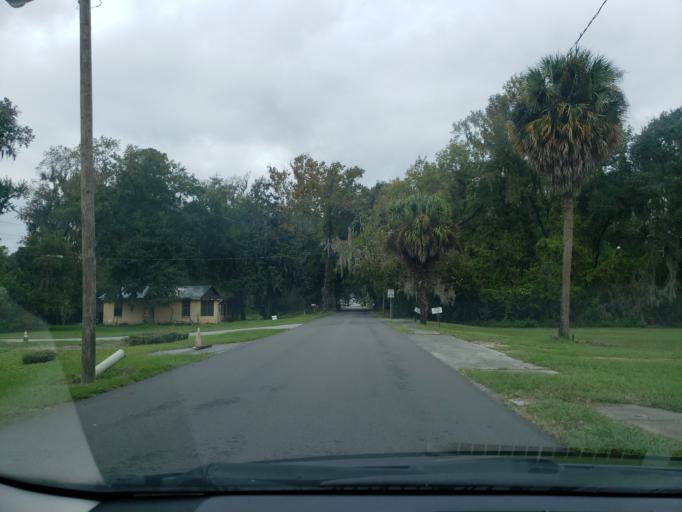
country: US
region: Georgia
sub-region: Chatham County
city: Thunderbolt
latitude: 32.0355
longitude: -81.0607
